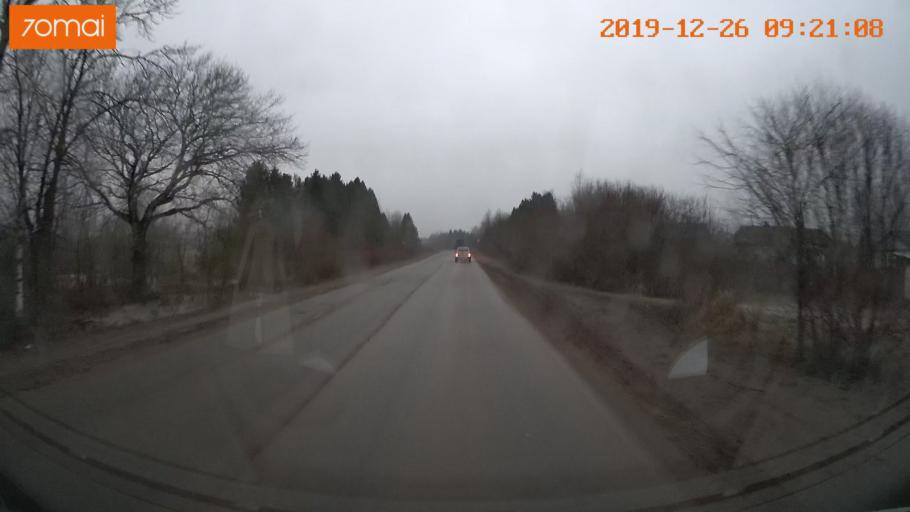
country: RU
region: Vologda
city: Gryazovets
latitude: 58.9678
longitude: 40.2261
